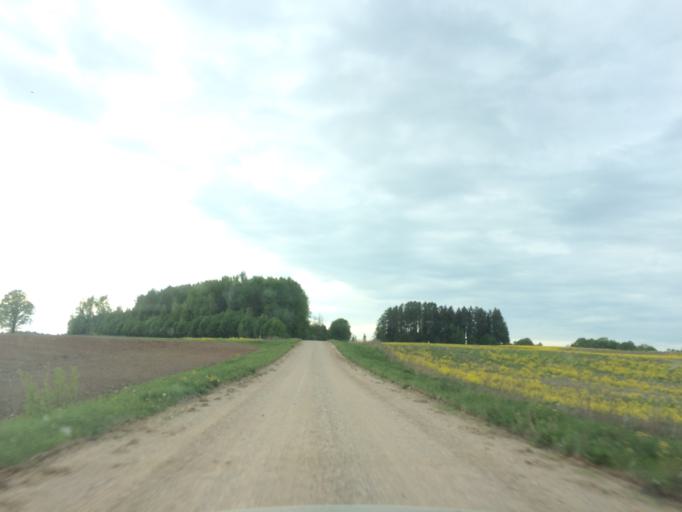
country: LV
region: Ludzas Rajons
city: Ludza
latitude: 56.5984
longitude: 27.5219
